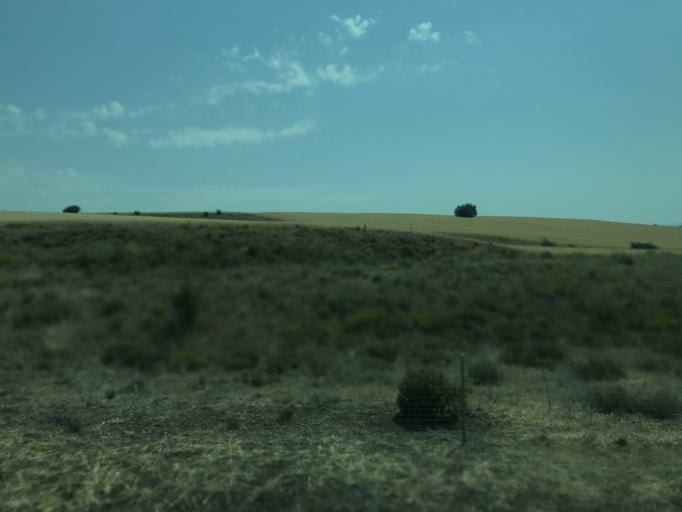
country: ES
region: Castille and Leon
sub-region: Provincia de Segovia
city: Fresno de la Fuente
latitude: 41.3791
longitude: -3.6447
